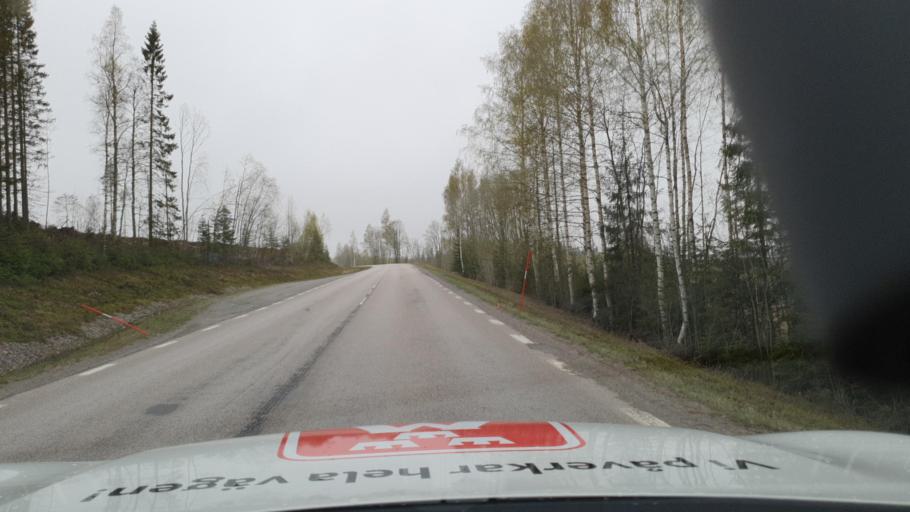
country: SE
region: Vaesterbotten
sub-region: Vannas Kommun
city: Vaennaes
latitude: 63.7891
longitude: 19.8252
